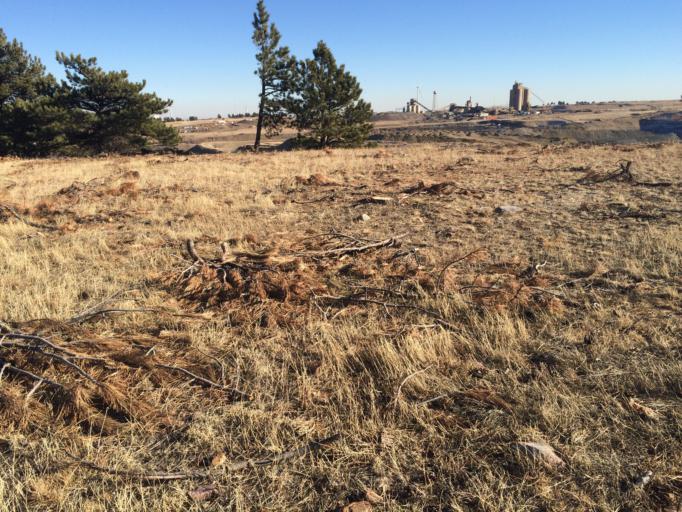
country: US
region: Colorado
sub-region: Boulder County
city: Superior
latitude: 39.9150
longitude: -105.2490
